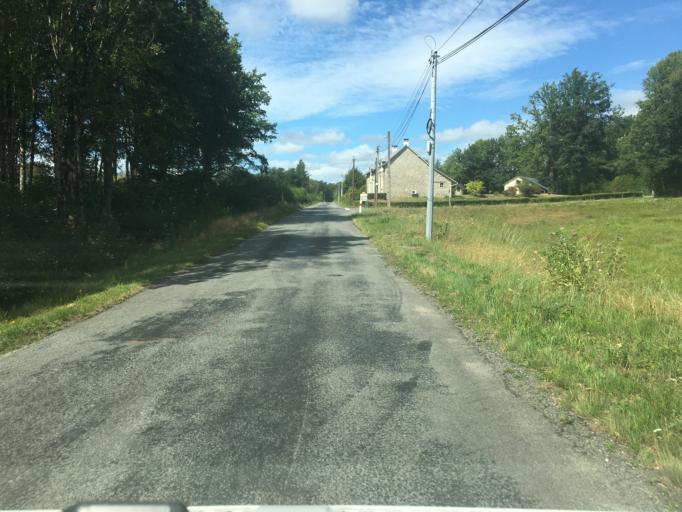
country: FR
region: Auvergne
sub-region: Departement du Cantal
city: Champagnac
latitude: 45.4243
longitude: 2.3756
